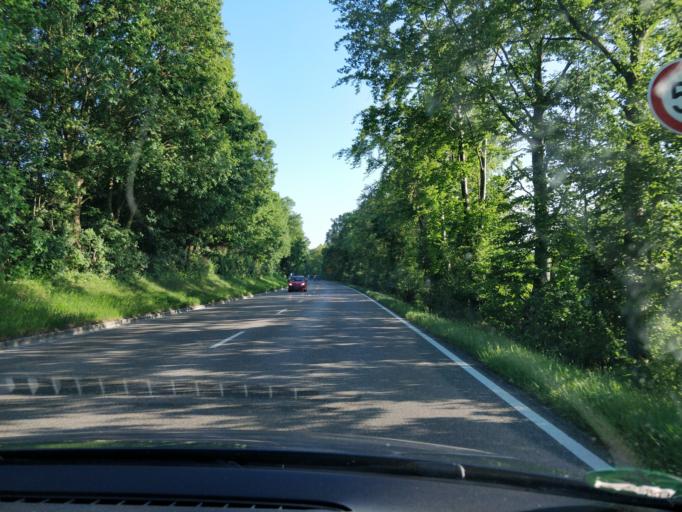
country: DE
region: Bavaria
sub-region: Swabia
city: Noerdlingen
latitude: 48.8427
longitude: 10.4804
